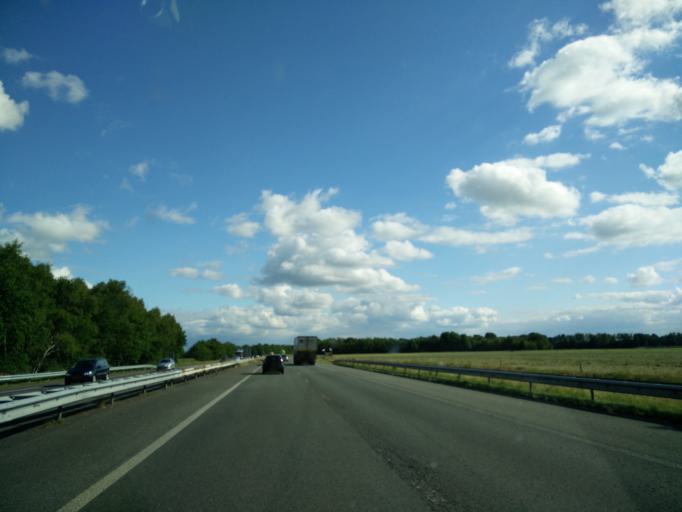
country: NL
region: Drenthe
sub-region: Gemeente Tynaarlo
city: Tynaarlo
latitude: 53.1100
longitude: 6.6116
